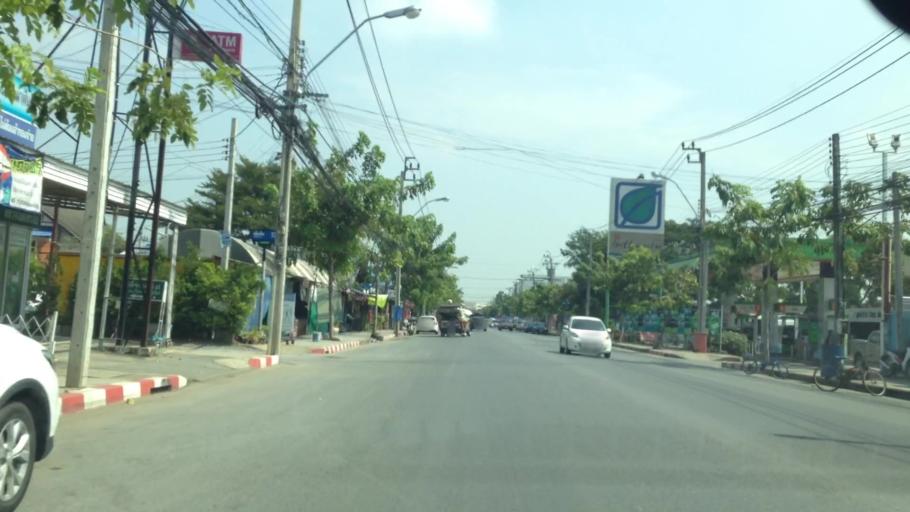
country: TH
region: Bangkok
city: Bang Khen
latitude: 13.8997
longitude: 100.6324
